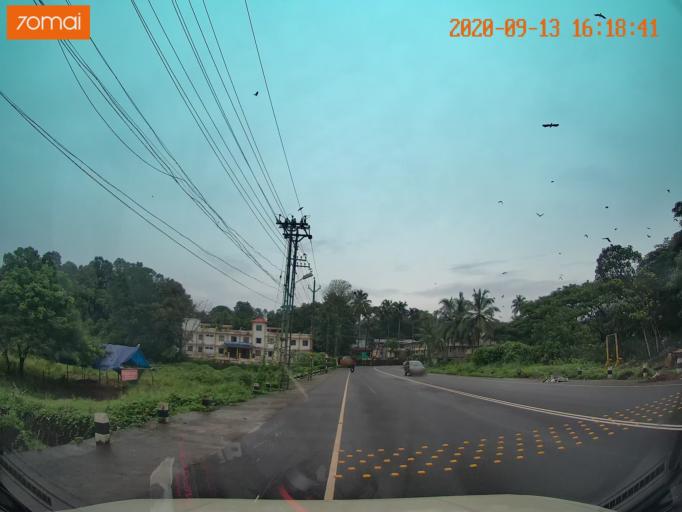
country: IN
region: Kerala
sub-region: Kottayam
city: Lalam
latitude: 9.7039
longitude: 76.6613
